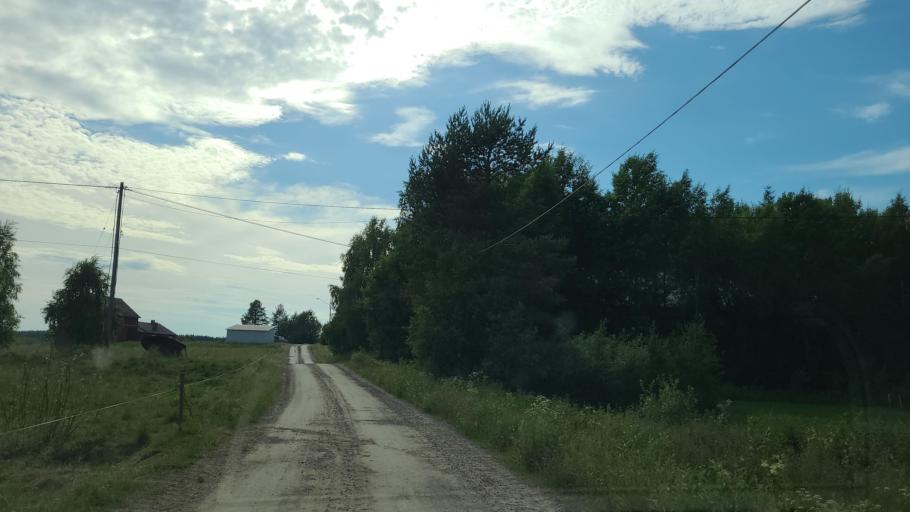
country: SE
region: Vaesterbotten
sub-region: Robertsfors Kommun
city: Robertsfors
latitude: 64.1567
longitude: 20.9212
